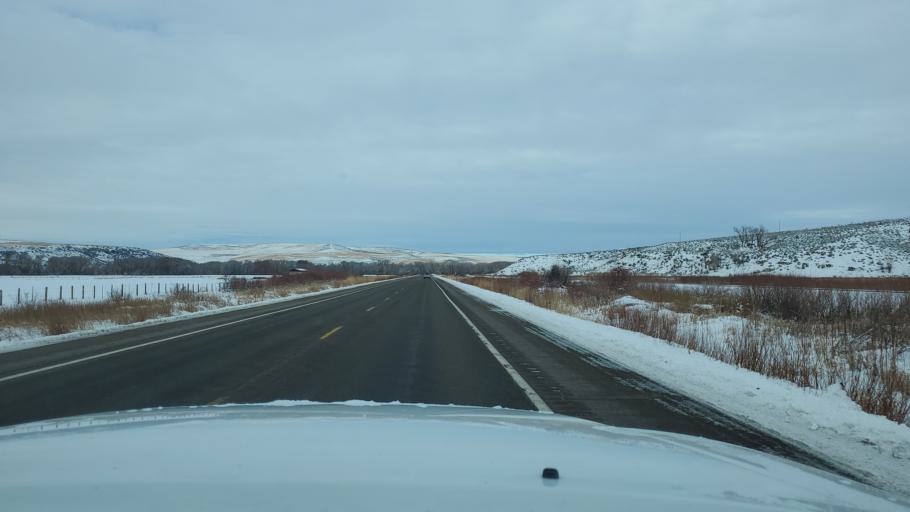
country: US
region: Colorado
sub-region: Routt County
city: Hayden
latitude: 40.4938
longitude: -107.3575
